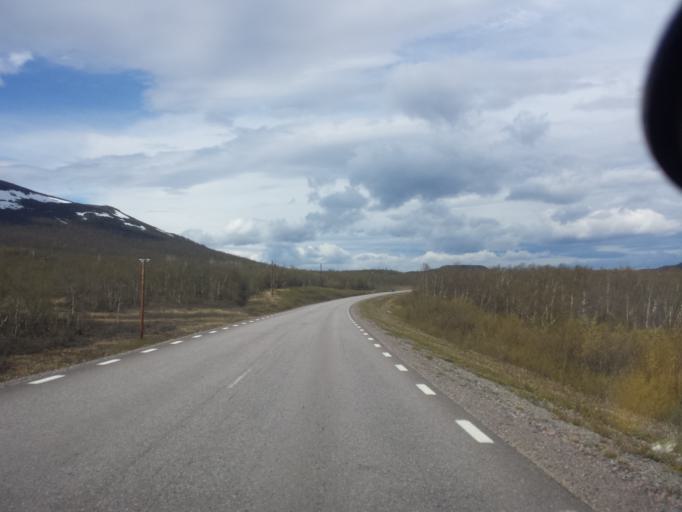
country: SE
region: Norrbotten
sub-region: Kiruna Kommun
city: Kiruna
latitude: 68.1620
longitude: 19.7796
